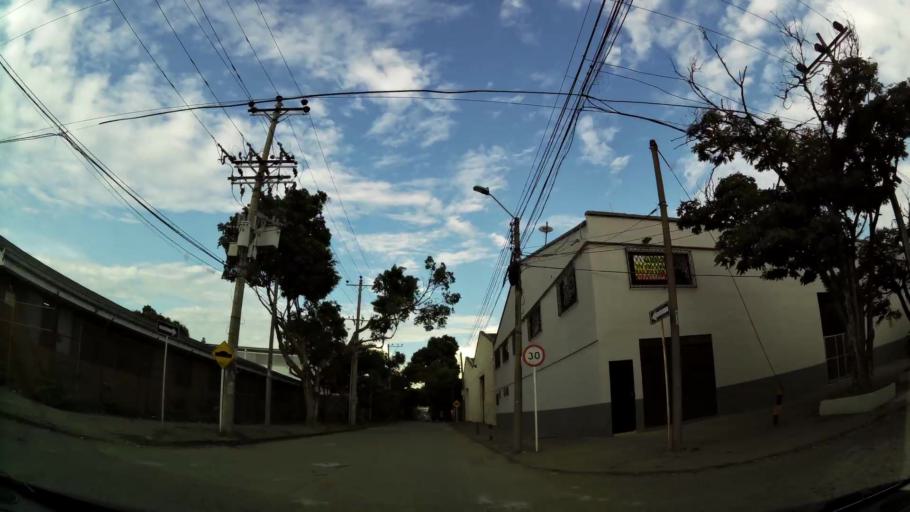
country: CO
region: Valle del Cauca
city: Cali
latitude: 3.4612
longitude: -76.5120
